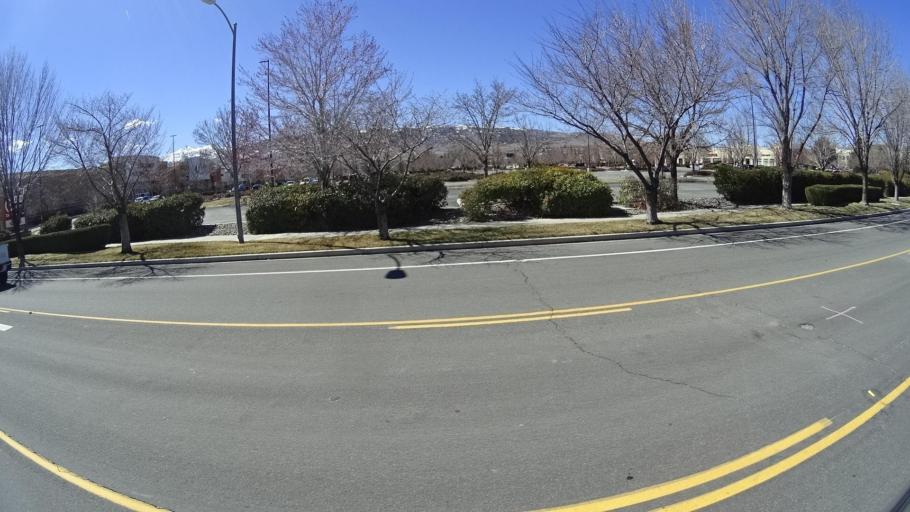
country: US
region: Nevada
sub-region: Washoe County
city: Reno
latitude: 39.4649
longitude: -119.7781
